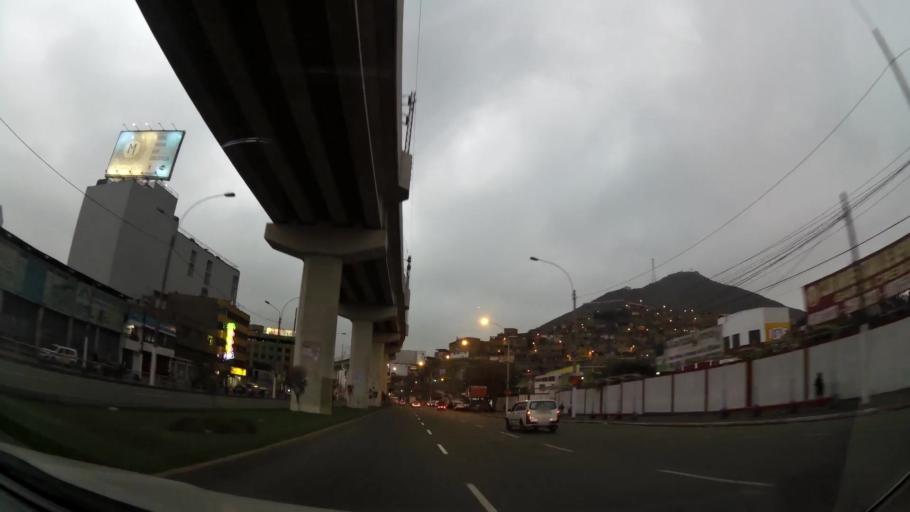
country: PE
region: Lima
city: Lima
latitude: -12.0298
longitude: -77.0120
